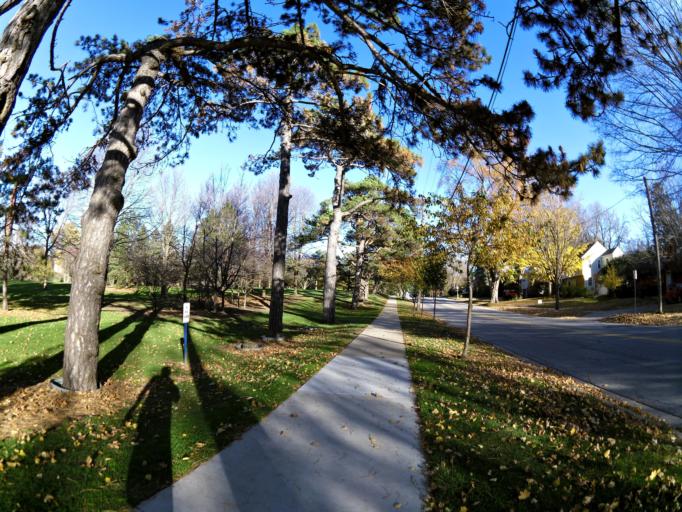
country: US
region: Minnesota
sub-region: Olmsted County
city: Rochester
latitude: 44.0172
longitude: -92.4805
